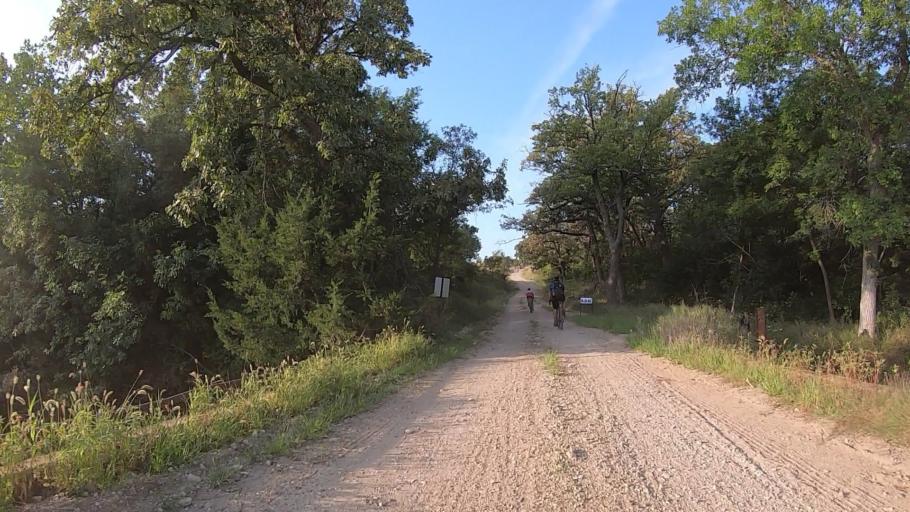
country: US
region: Kansas
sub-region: Marshall County
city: Blue Rapids
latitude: 39.7204
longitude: -96.8060
